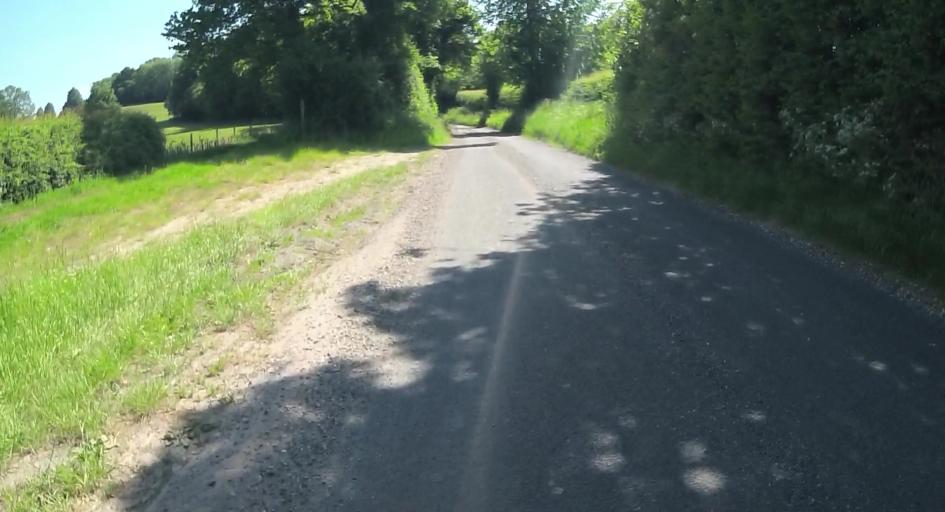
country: GB
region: England
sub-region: Hampshire
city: Kingsclere
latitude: 51.3282
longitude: -1.2899
